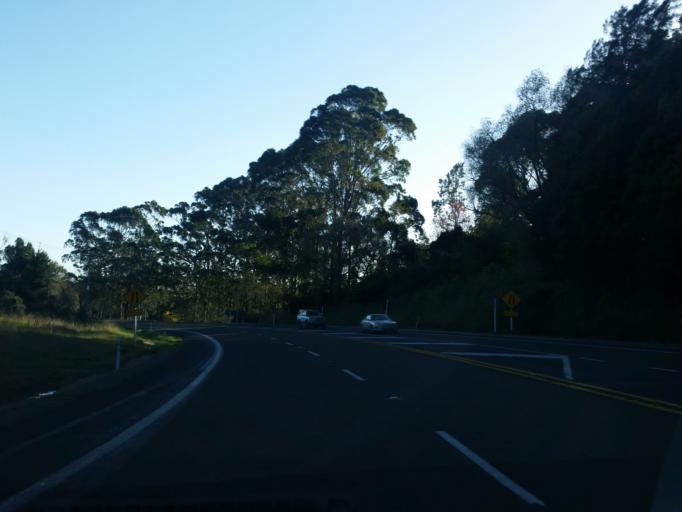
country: NZ
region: Bay of Plenty
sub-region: Western Bay of Plenty District
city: Katikati
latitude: -37.6293
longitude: 175.9572
